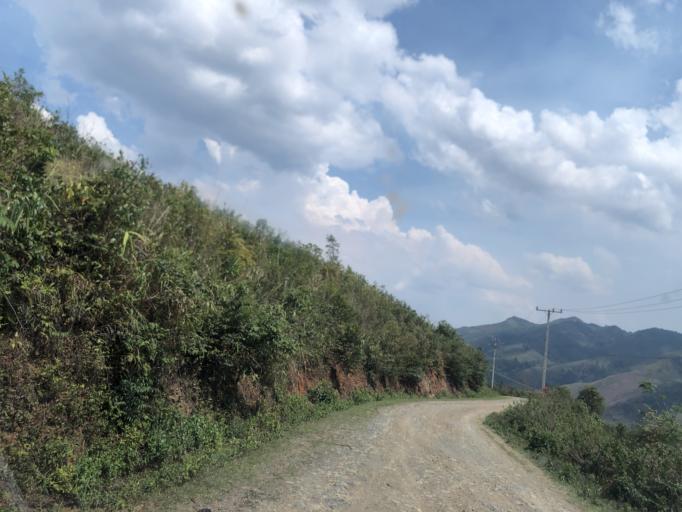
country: LA
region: Phongsali
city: Phongsali
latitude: 21.4079
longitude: 102.2374
